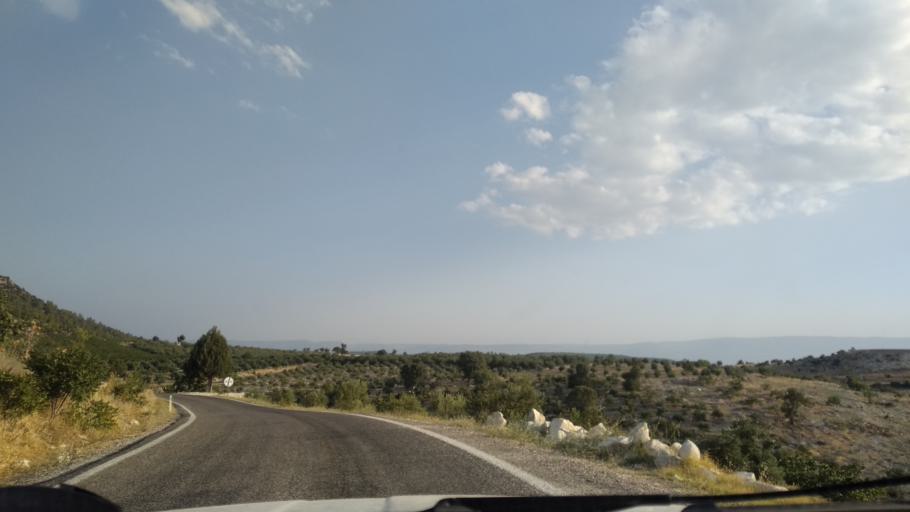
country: TR
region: Mersin
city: Sarikavak
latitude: 36.5680
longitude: 33.6333
